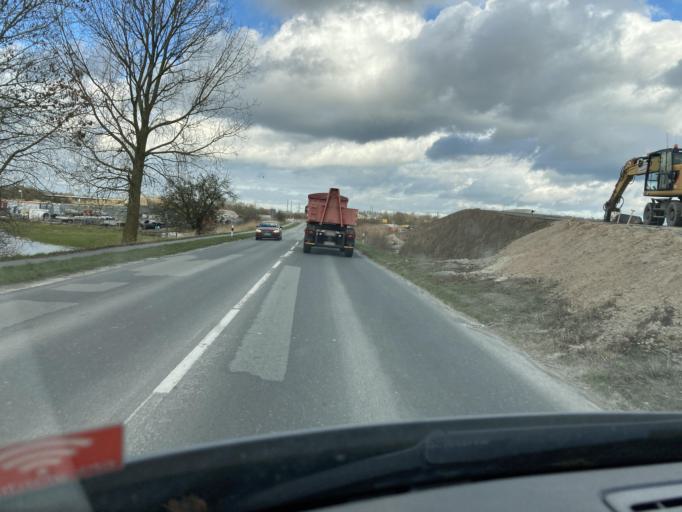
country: DE
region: Lower Saxony
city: Sande
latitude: 53.5145
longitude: 8.0229
